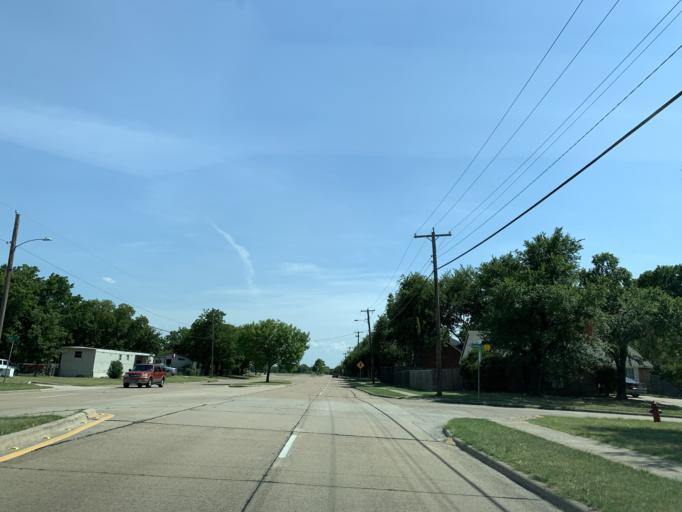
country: US
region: Texas
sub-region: Dallas County
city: Cedar Hill
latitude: 32.6516
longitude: -97.0148
